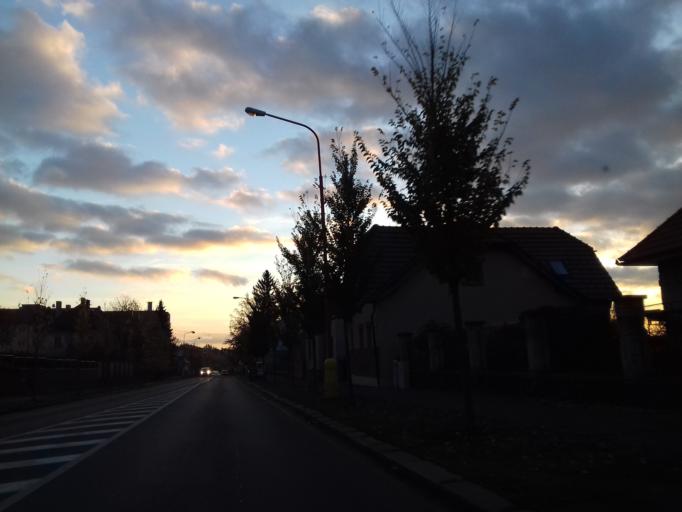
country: CZ
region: Pardubicky
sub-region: Okres Chrudim
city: Hlinsko
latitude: 49.7647
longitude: 15.9138
